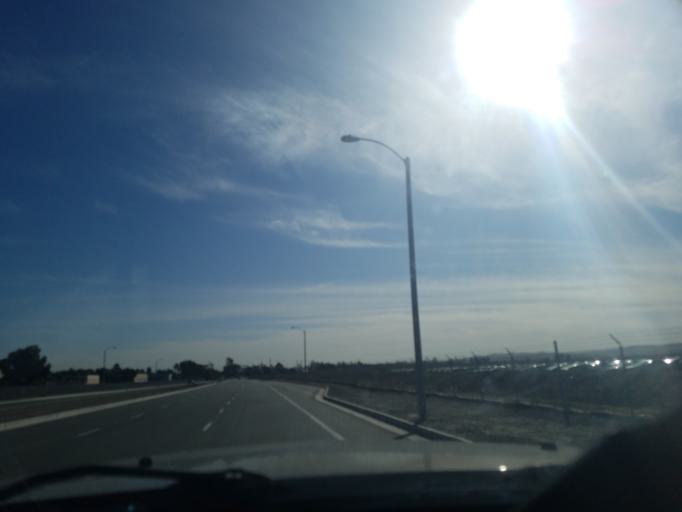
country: US
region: California
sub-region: Orange County
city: Tustin
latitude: 33.7128
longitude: -117.8135
